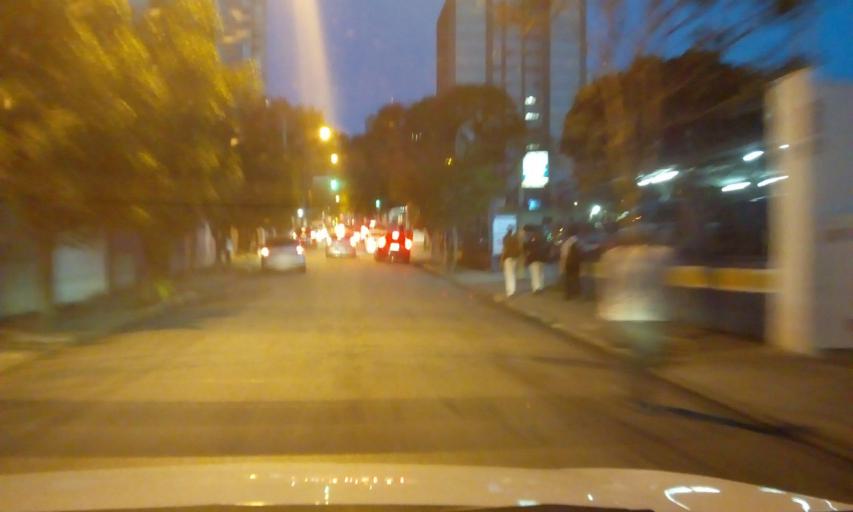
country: BR
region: Sao Paulo
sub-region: Sao Paulo
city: Sao Paulo
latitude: -23.5989
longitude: -46.6790
